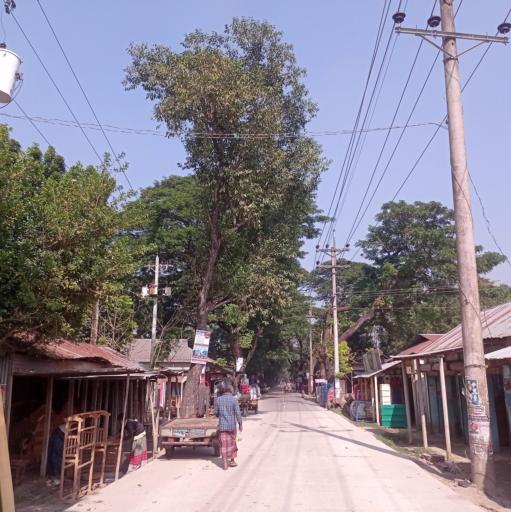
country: BD
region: Dhaka
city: Narsingdi
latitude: 24.0477
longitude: 90.6808
